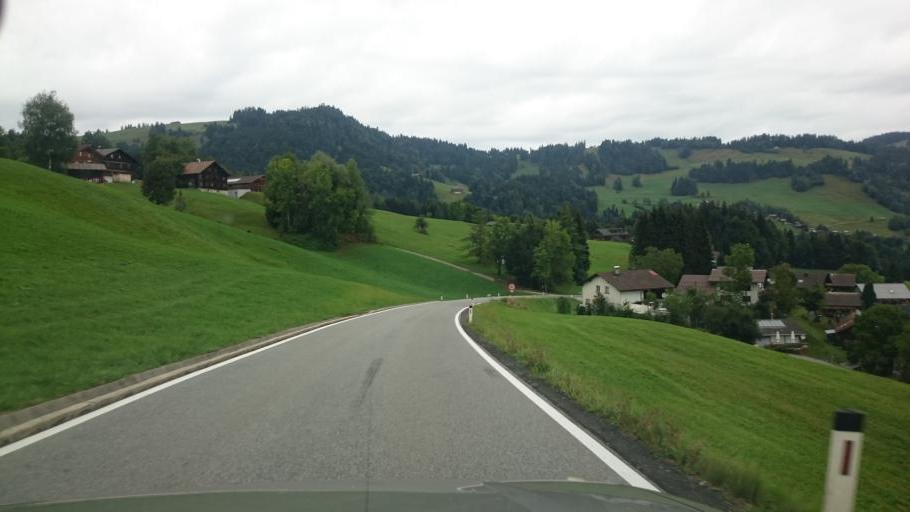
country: AT
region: Vorarlberg
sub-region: Politischer Bezirk Bregenz
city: Andelsbuch
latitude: 47.4140
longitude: 9.8389
